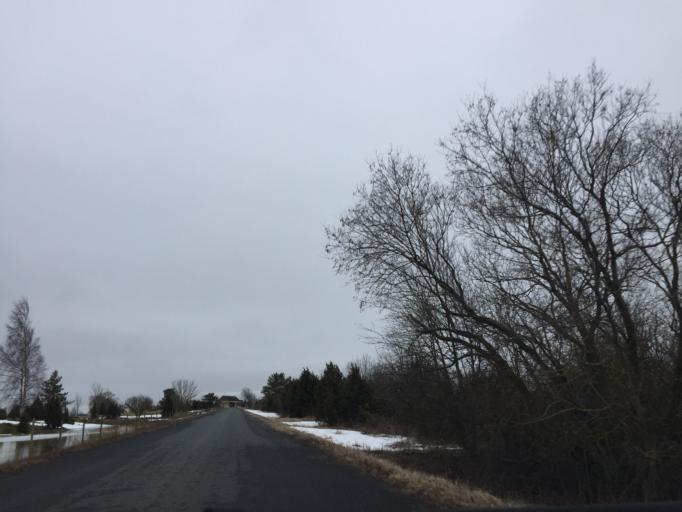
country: EE
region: Laeaene
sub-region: Haapsalu linn
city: Haapsalu
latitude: 58.7693
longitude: 23.4560
